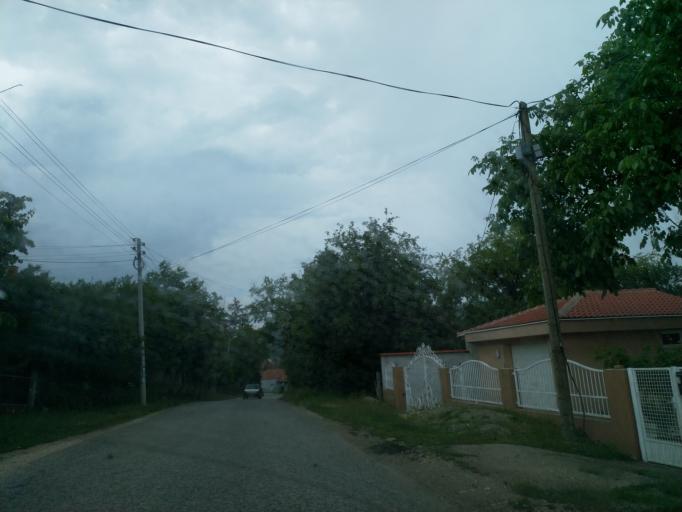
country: RS
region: Central Serbia
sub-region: Borski Okrug
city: Bor
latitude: 44.0058
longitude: 21.9834
